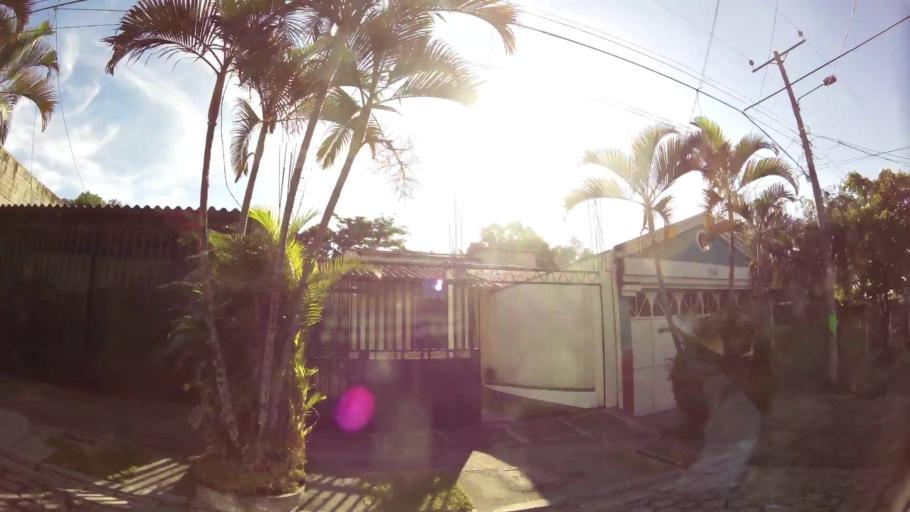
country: SV
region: La Libertad
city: Santa Tecla
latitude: 13.6847
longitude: -89.2842
